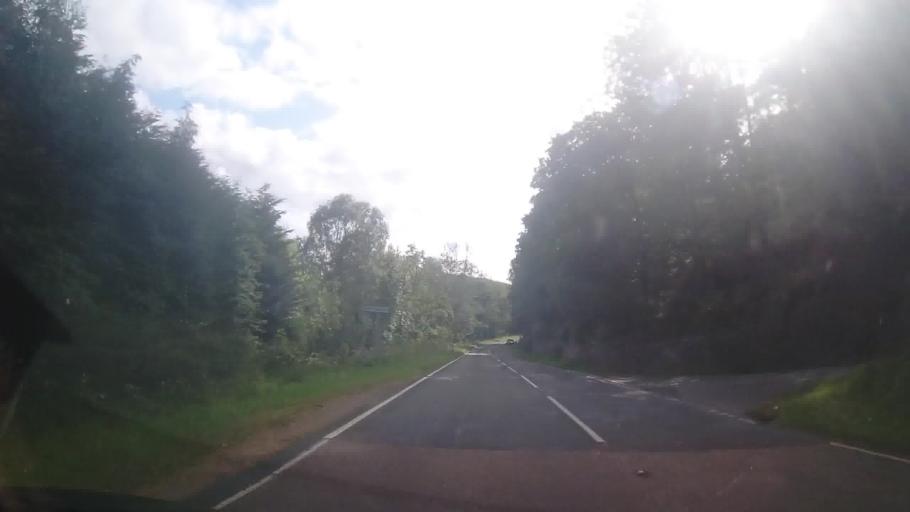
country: GB
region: Wales
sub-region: Gwynedd
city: Barmouth
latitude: 52.7432
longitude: -4.0047
